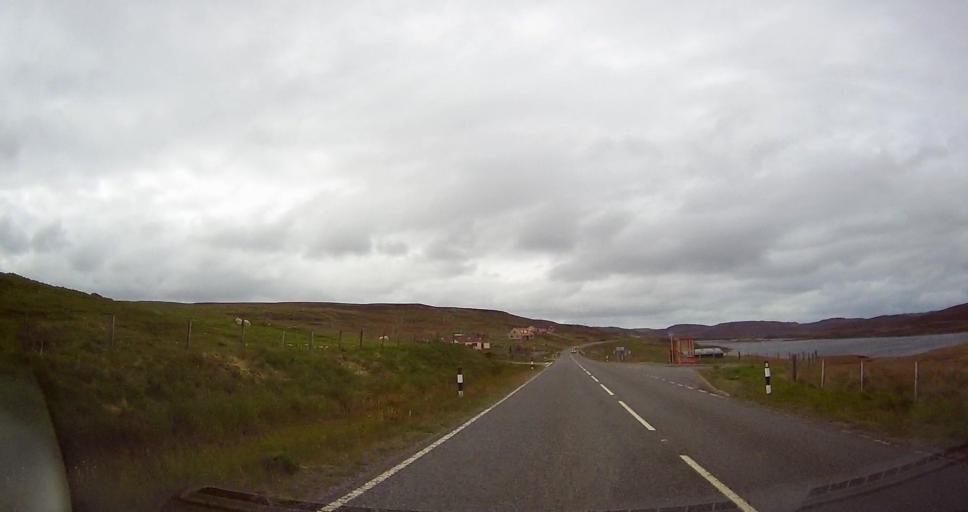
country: GB
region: Scotland
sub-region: Shetland Islands
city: Lerwick
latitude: 60.2543
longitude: -1.4565
